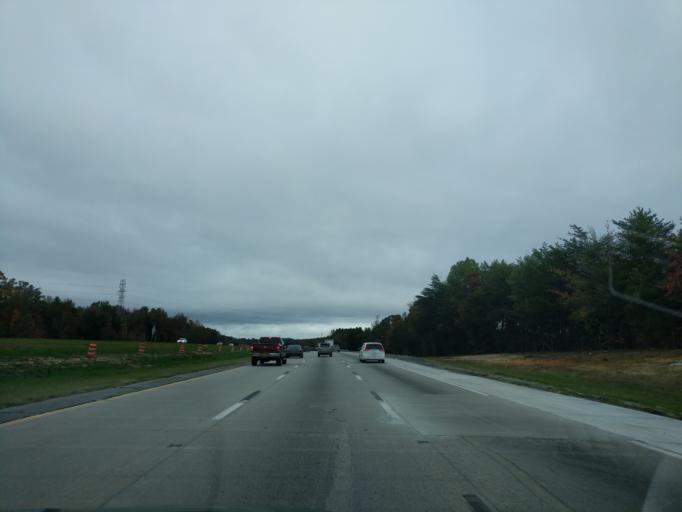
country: US
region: North Carolina
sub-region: Guilford County
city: Jamestown
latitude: 35.9602
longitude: -79.8947
